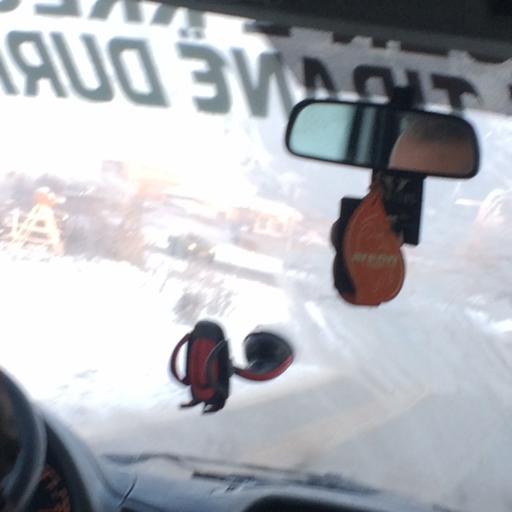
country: XK
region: Pristina
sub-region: Komuna e Drenasit
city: Glogovac
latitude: 42.5879
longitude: 20.8937
